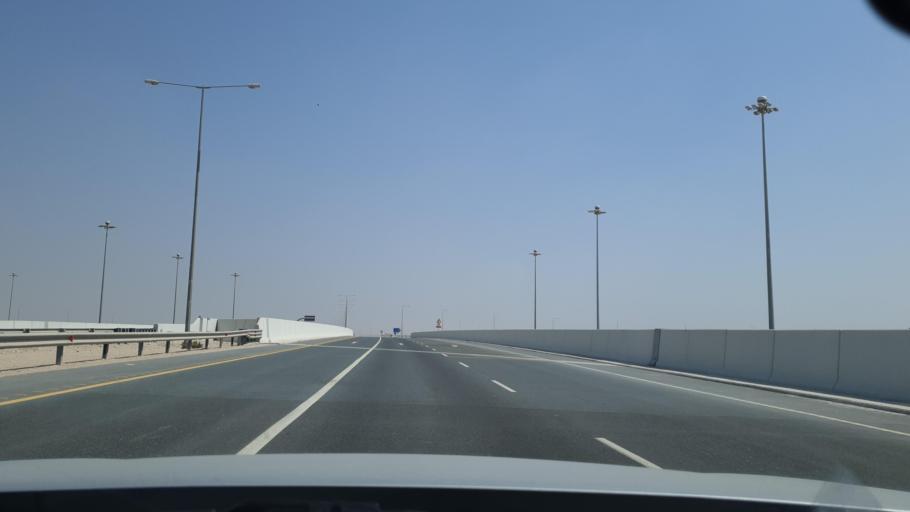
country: QA
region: Baladiyat az Za`ayin
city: Az Za`ayin
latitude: 25.6169
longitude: 51.3668
